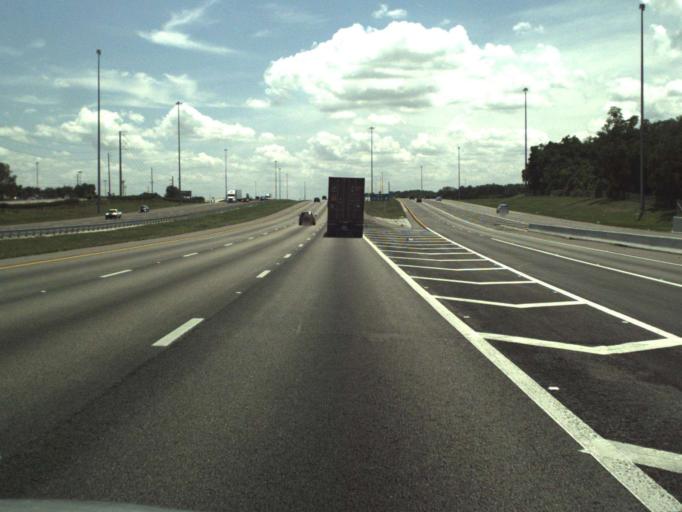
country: US
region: Florida
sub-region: Seminole County
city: Lake Mary
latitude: 28.8077
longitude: -81.3400
